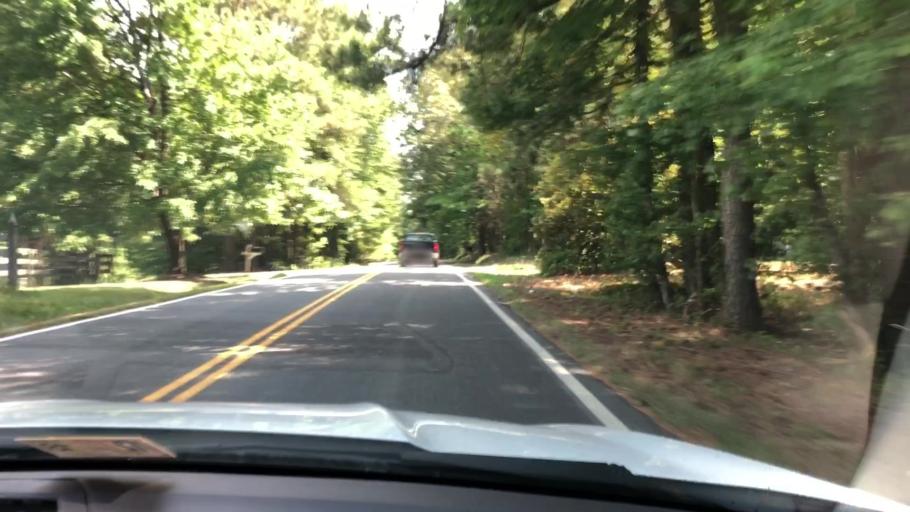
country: US
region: Virginia
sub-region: King William County
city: West Point
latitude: 37.4930
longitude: -76.8152
